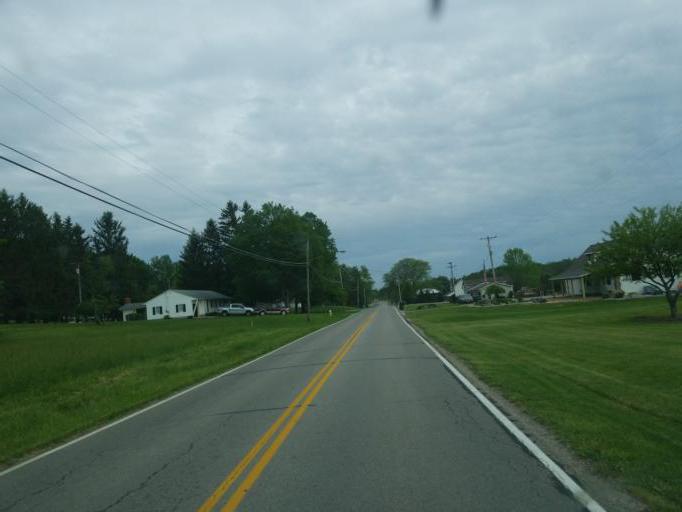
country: US
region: Ohio
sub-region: Richland County
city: Ontario
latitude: 40.7660
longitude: -82.6322
